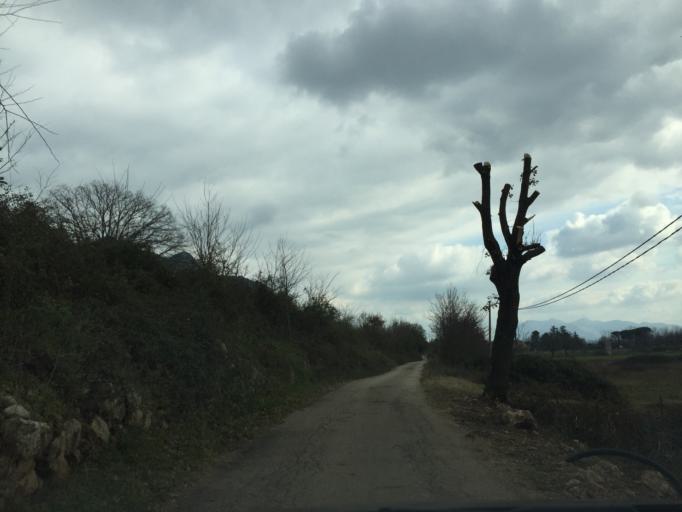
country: IT
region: Latium
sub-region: Provincia di Frosinone
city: Villa Santa Lucia
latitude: 41.4895
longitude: 13.7859
